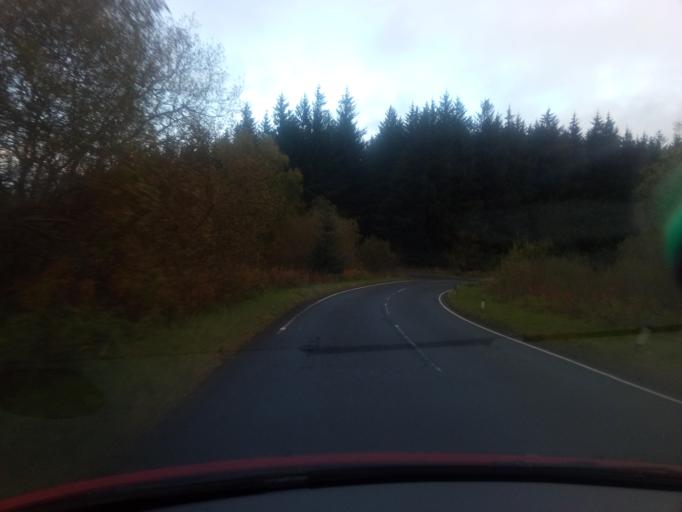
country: GB
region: Scotland
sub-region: The Scottish Borders
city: Hawick
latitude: 55.3310
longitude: -2.6509
